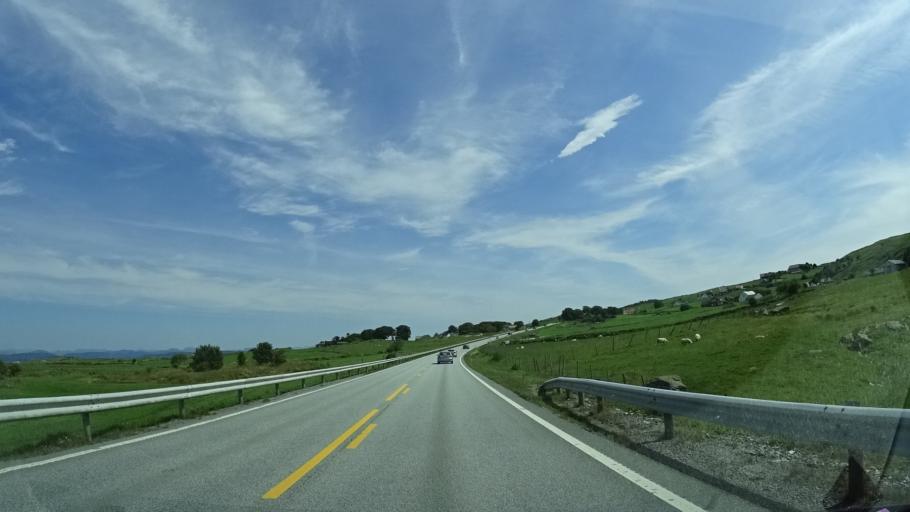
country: NO
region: Rogaland
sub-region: Rennesoy
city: Vikevag
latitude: 59.1274
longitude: 5.6271
